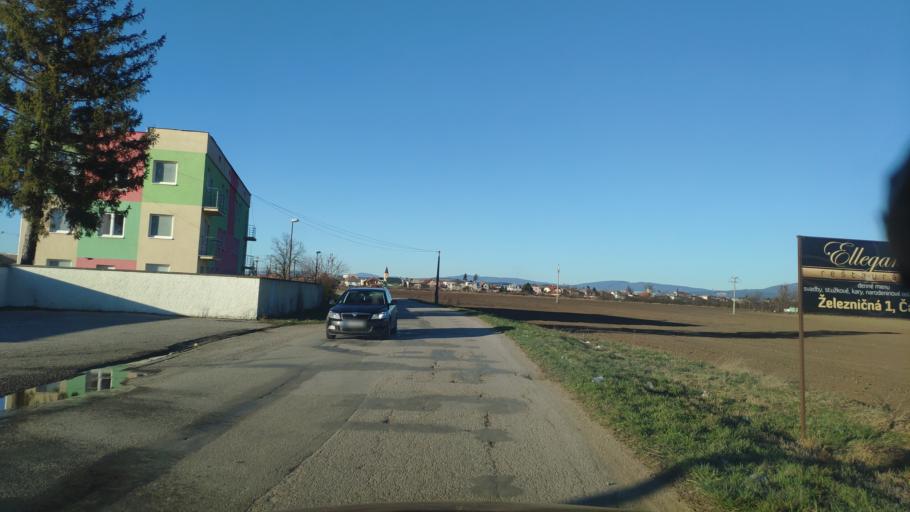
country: SK
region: Kosicky
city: Kosice
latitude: 48.6002
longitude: 21.3214
